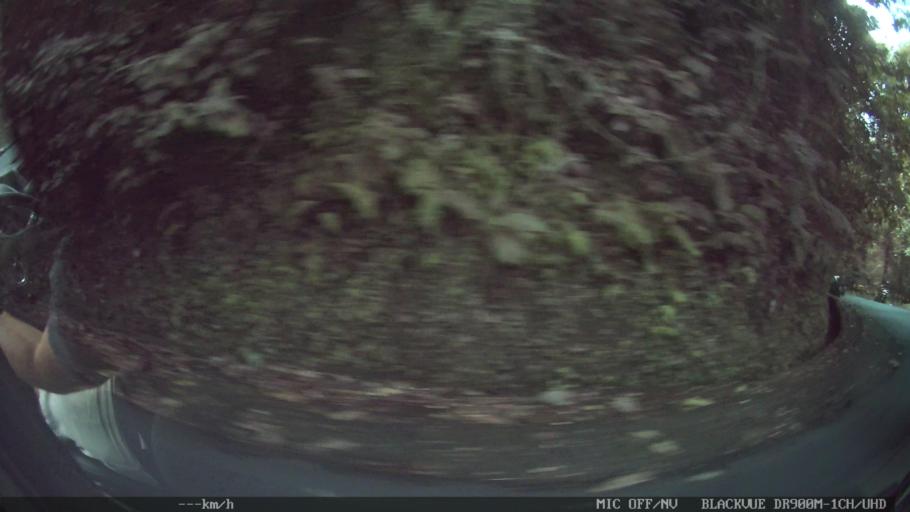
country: ID
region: Bali
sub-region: Kabupaten Gianyar
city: Ubud
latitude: -8.5080
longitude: 115.2781
